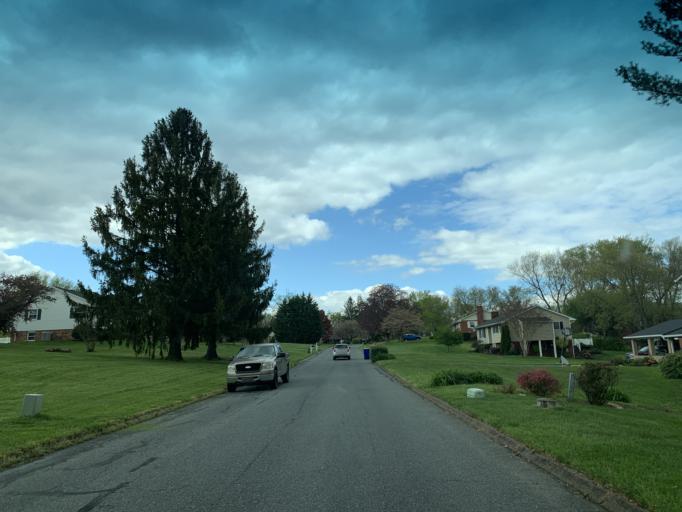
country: US
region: Maryland
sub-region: Harford County
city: Pleasant Hills
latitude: 39.4985
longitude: -76.3639
